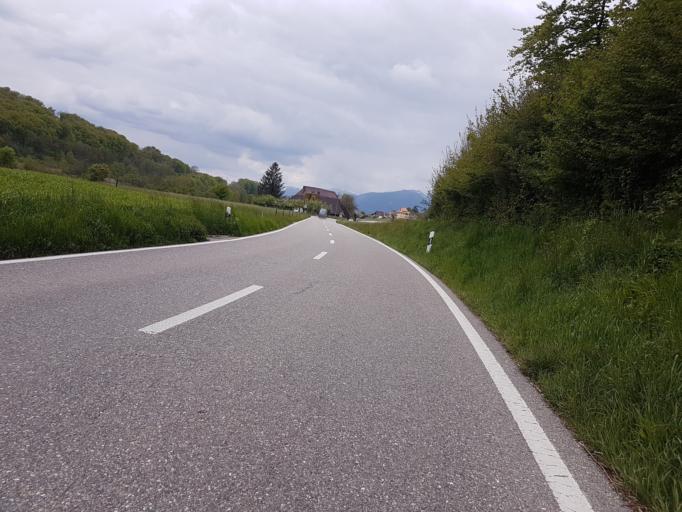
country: CH
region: Bern
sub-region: Oberaargau
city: Niederbipp
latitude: 47.2346
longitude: 7.7003
